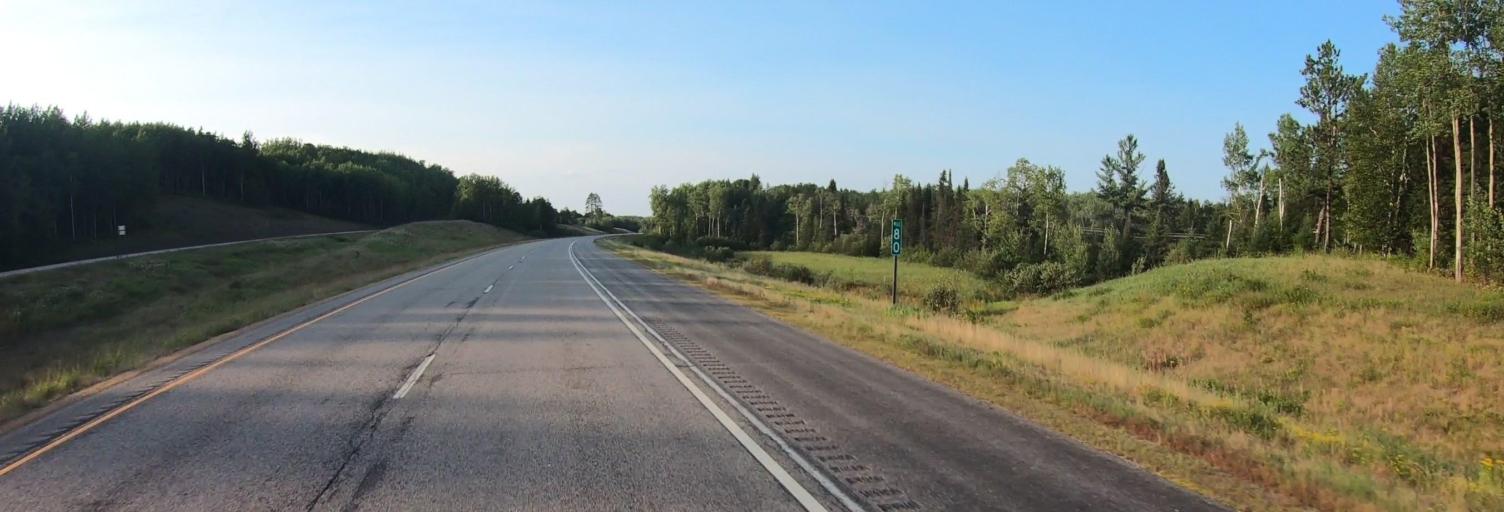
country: US
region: Minnesota
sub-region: Saint Louis County
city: Mountain Iron
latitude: 47.6813
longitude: -92.6377
